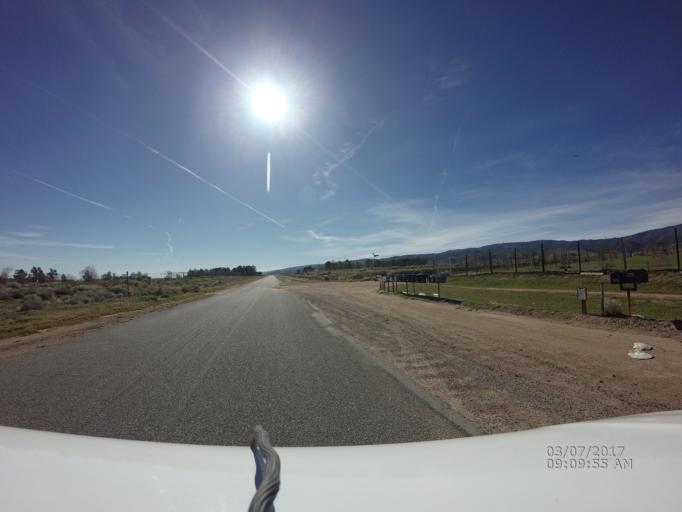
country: US
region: California
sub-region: Los Angeles County
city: Green Valley
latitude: 34.7788
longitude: -118.5795
